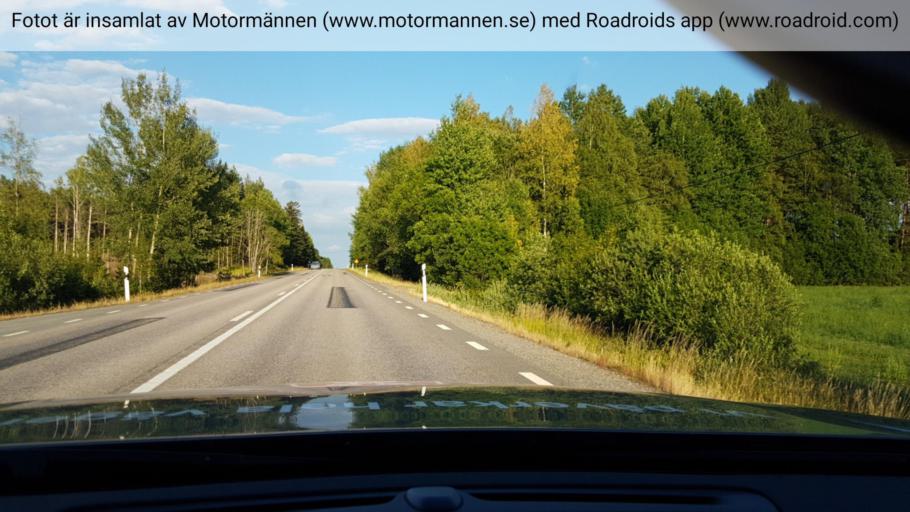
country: SE
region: Uppsala
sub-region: Heby Kommun
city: Morgongava
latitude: 59.8977
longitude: 17.1022
